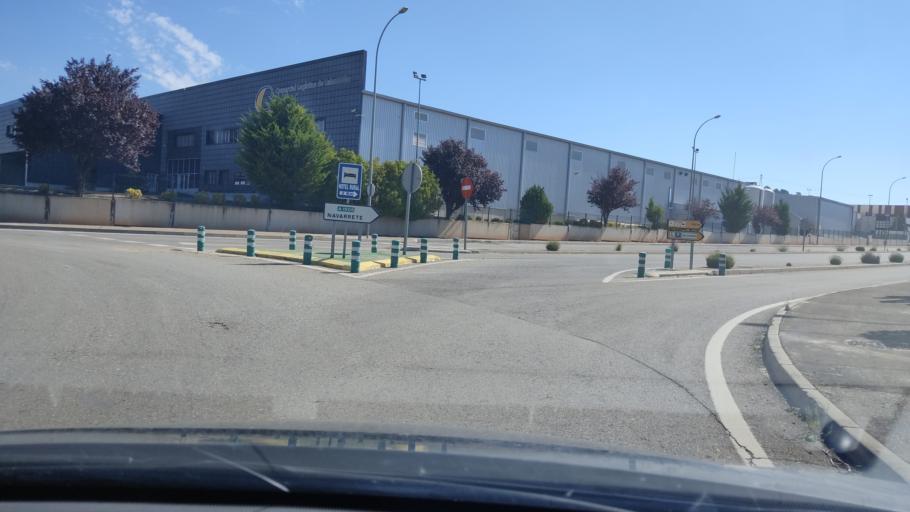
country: ES
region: Aragon
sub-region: Provincia de Teruel
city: Calamocha
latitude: 40.9175
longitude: -1.2833
